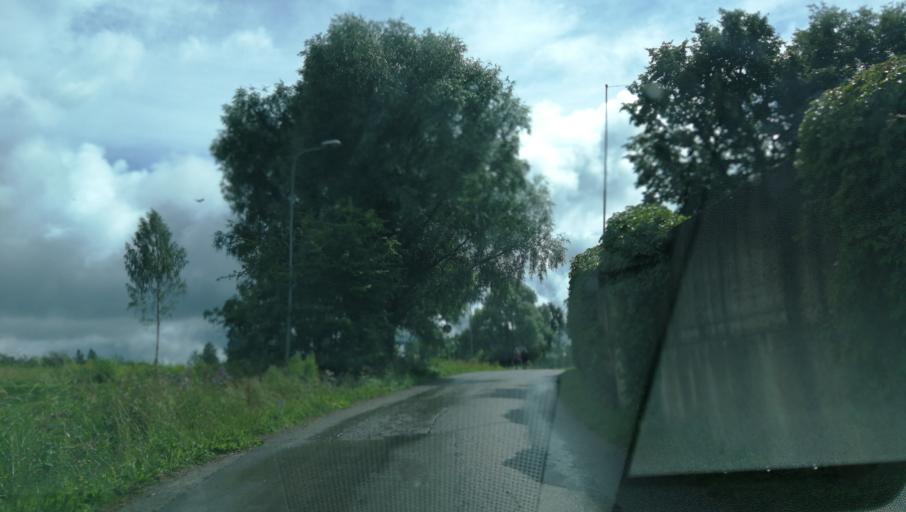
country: LV
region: Cesu Rajons
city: Cesis
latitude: 57.3020
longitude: 25.2632
